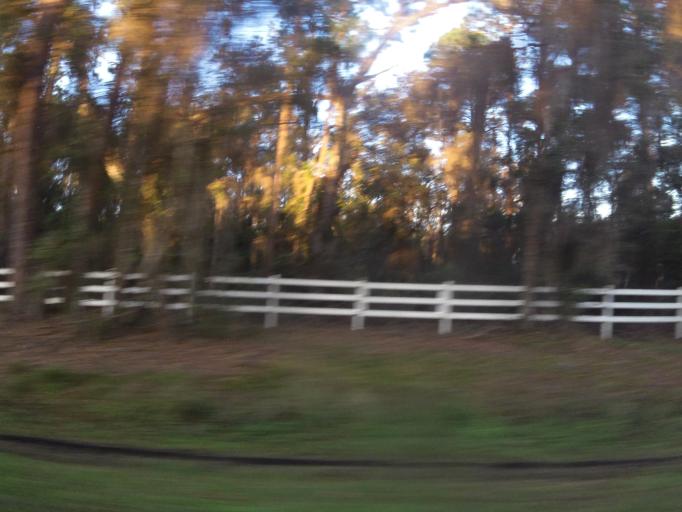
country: US
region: Florida
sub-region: Clay County
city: Green Cove Springs
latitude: 29.9027
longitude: -81.5876
